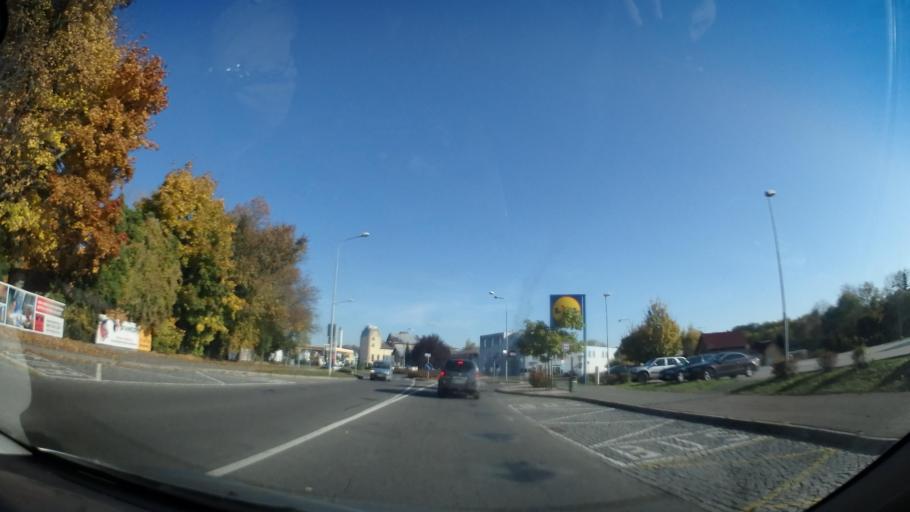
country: CZ
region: Pardubicky
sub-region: Okres Chrudim
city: Chrudim
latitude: 49.9556
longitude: 15.7972
